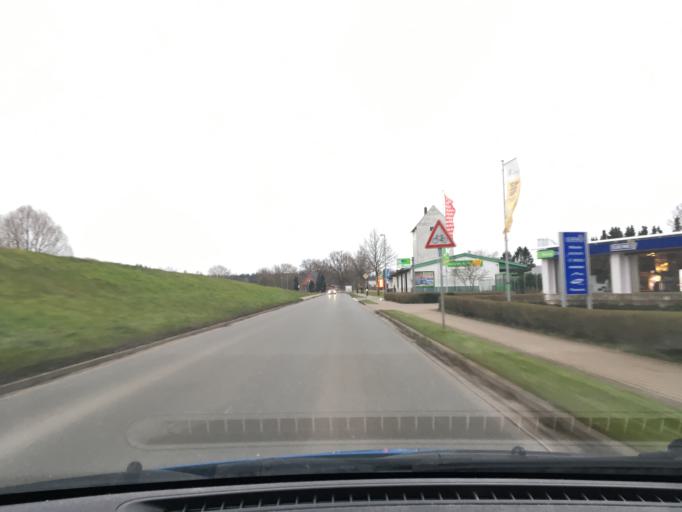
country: DE
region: Lower Saxony
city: Bleckede
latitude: 53.2873
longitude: 10.7388
